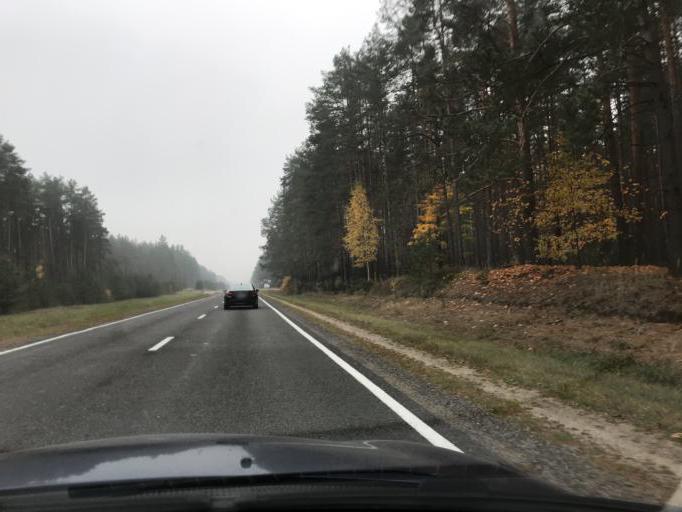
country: LT
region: Alytaus apskritis
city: Druskininkai
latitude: 53.8645
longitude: 23.8935
